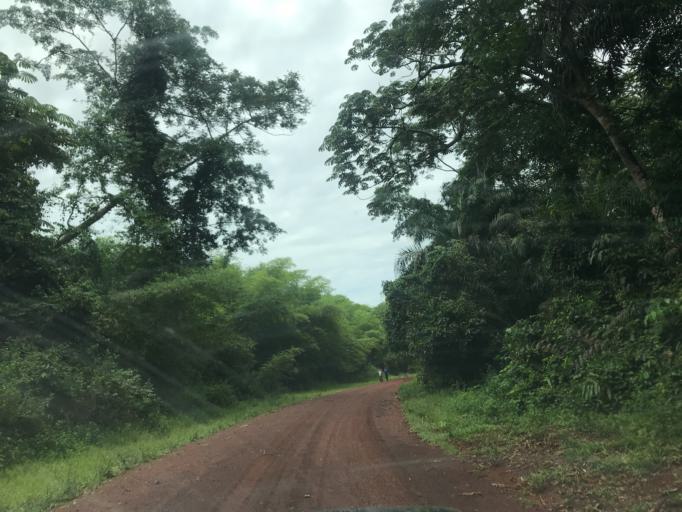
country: CD
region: Eastern Province
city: Buta
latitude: 2.3402
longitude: 24.9615
